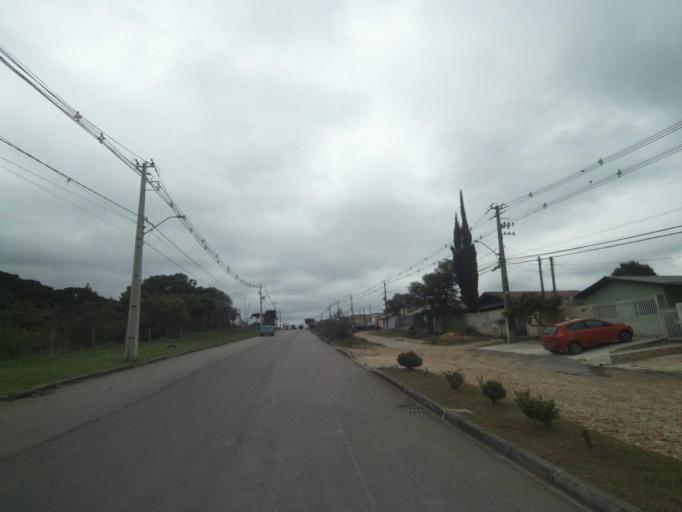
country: BR
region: Parana
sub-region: Araucaria
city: Araucaria
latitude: -25.5580
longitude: -49.3144
